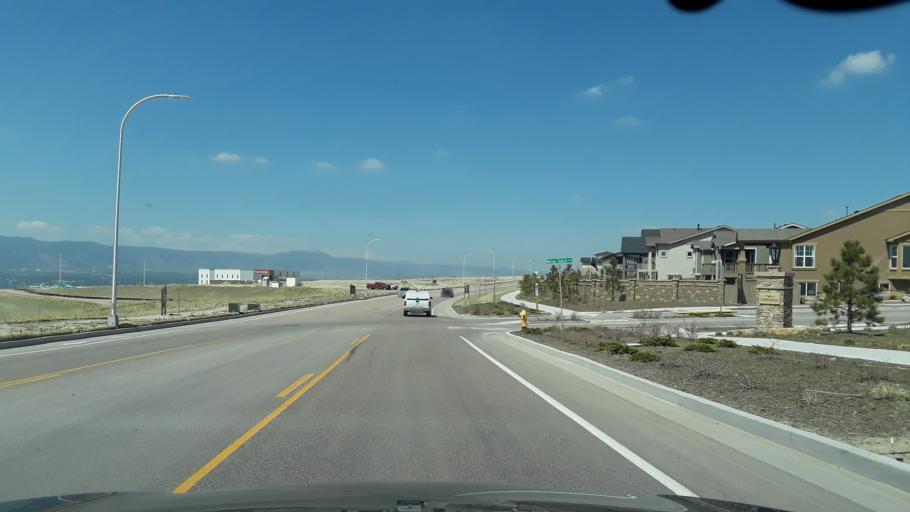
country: US
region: Colorado
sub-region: El Paso County
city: Black Forest
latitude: 38.9803
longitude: -104.7554
